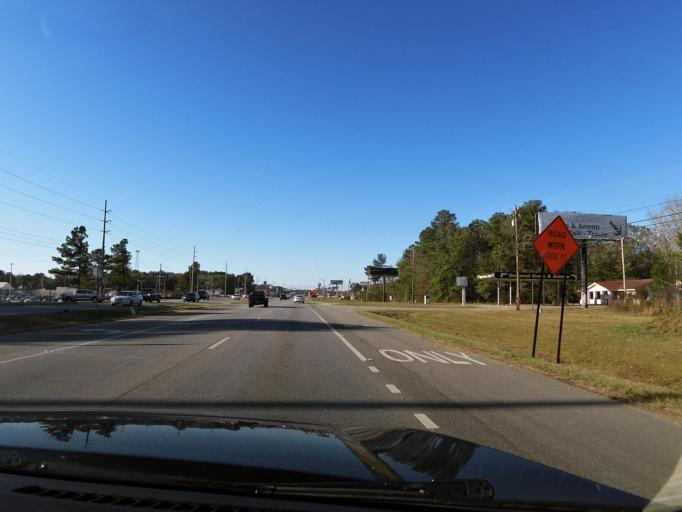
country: US
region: Alabama
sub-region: Houston County
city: Dothan
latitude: 31.2055
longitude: -85.4216
